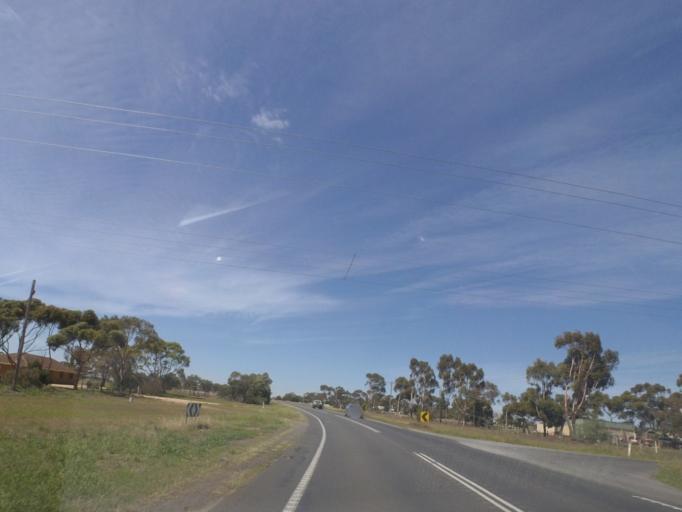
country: AU
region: Victoria
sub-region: Moorabool
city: Bacchus Marsh
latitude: -37.7189
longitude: 144.4509
